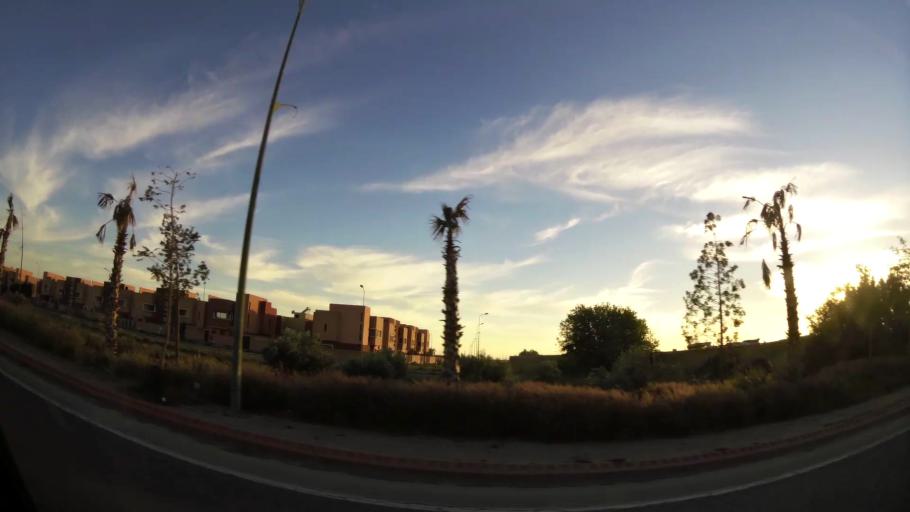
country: MA
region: Marrakech-Tensift-Al Haouz
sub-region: Marrakech
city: Marrakesh
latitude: 31.7645
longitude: -8.1183
